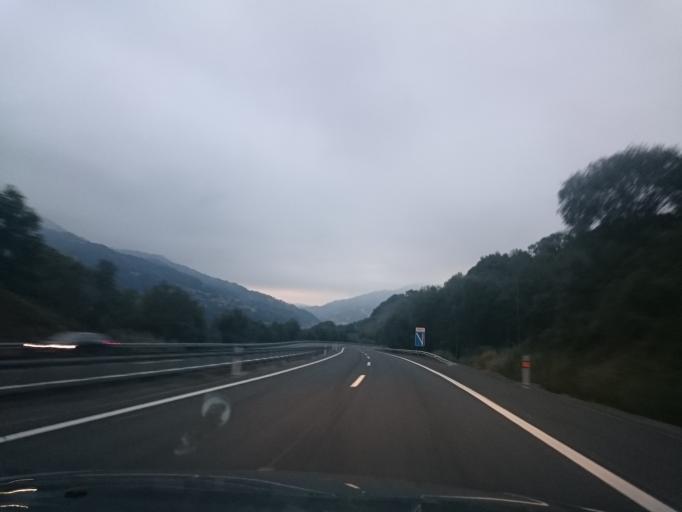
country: ES
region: Asturias
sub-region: Province of Asturias
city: Pola de Lena
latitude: 43.0839
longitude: -5.8249
